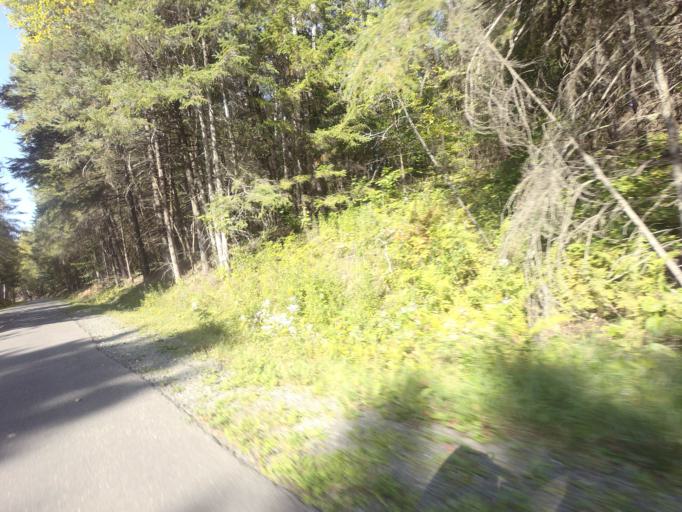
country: CA
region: Quebec
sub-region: Laurentides
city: Mont-Tremblant
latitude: 46.1278
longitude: -74.5736
